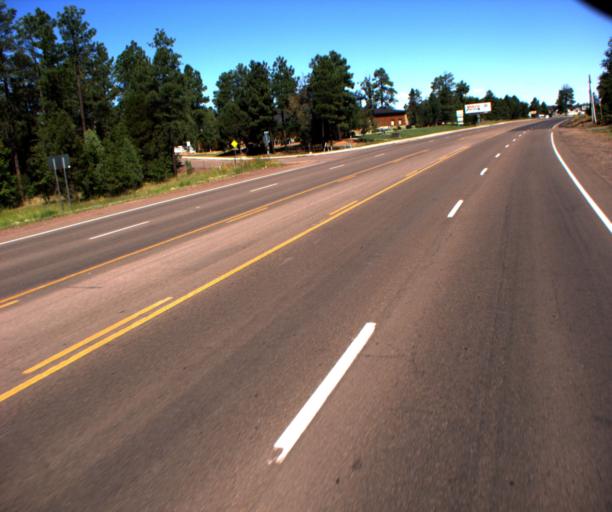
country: US
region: Arizona
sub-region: Navajo County
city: Lake of the Woods
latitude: 34.1830
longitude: -110.0145
